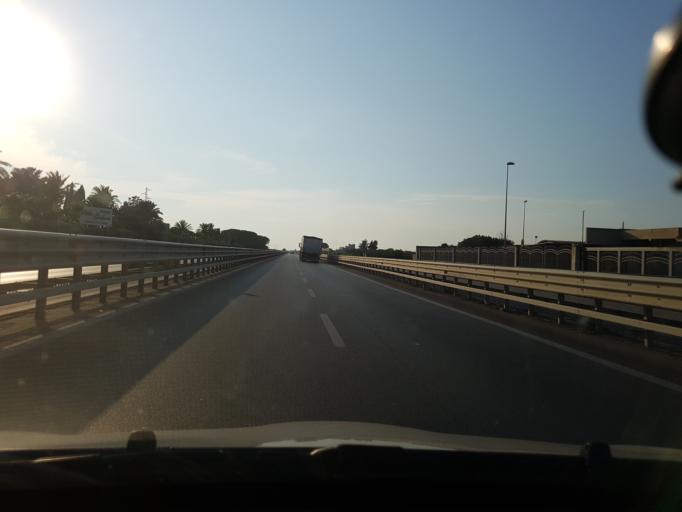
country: IT
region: Apulia
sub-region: Provincia di Foggia
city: Stornara
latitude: 41.3239
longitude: 15.7772
